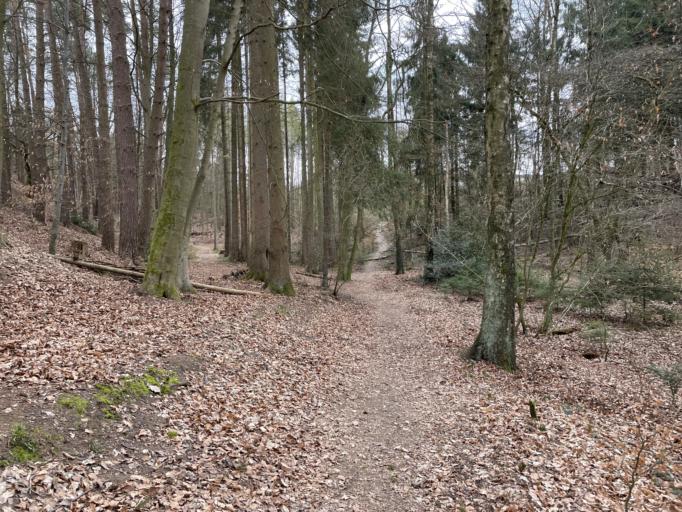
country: DE
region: North Rhine-Westphalia
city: Porta Westfalica
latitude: 52.2287
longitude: 8.9252
